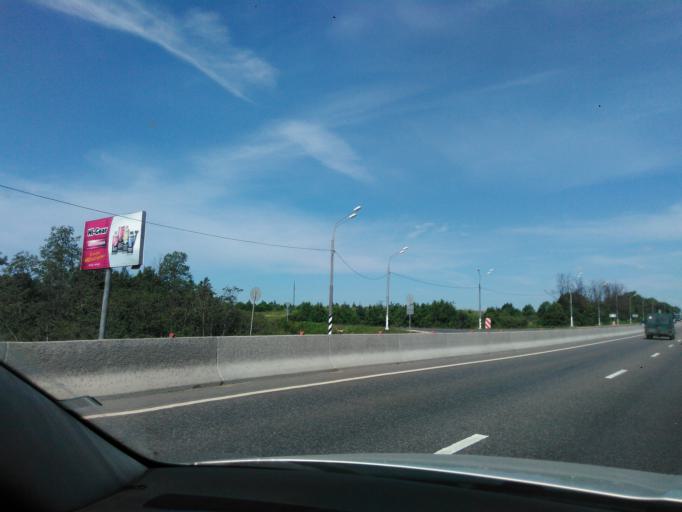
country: RU
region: Moskovskaya
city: Lozhki
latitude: 56.1086
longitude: 37.0926
